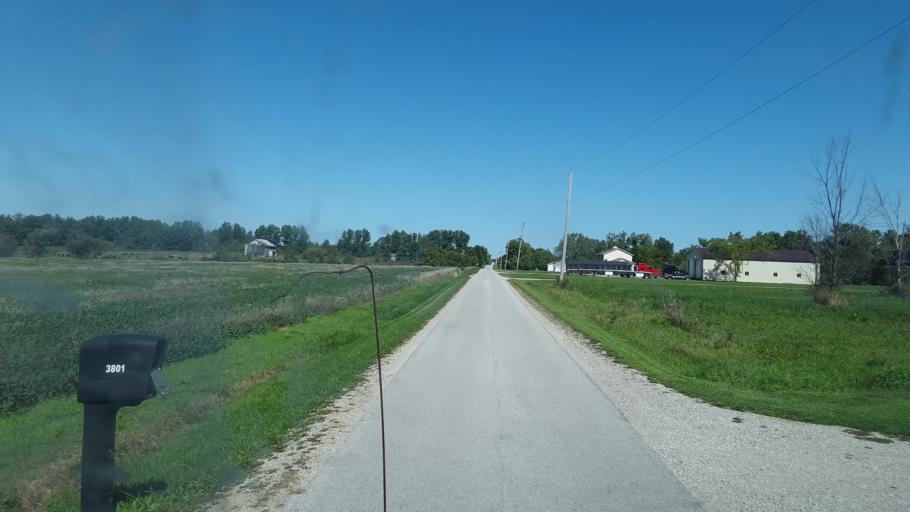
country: US
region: Ohio
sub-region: Sandusky County
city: Mount Carmel
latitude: 41.1775
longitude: -82.8995
